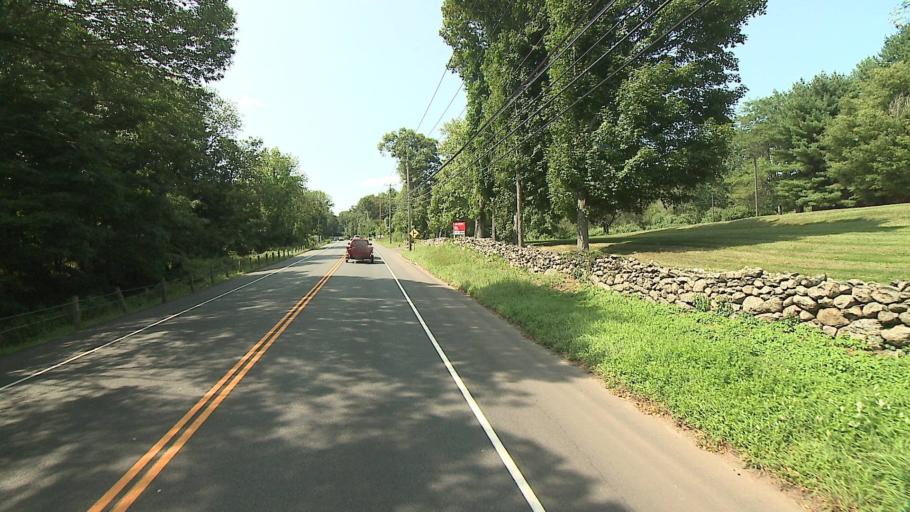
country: US
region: Connecticut
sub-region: Fairfield County
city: Newtown
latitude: 41.3786
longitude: -73.2785
